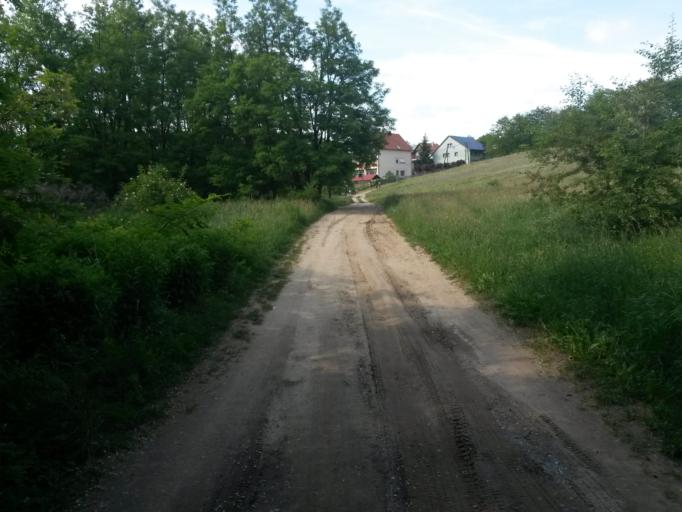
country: HU
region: Pest
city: Kerepes
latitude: 47.5697
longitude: 19.2755
